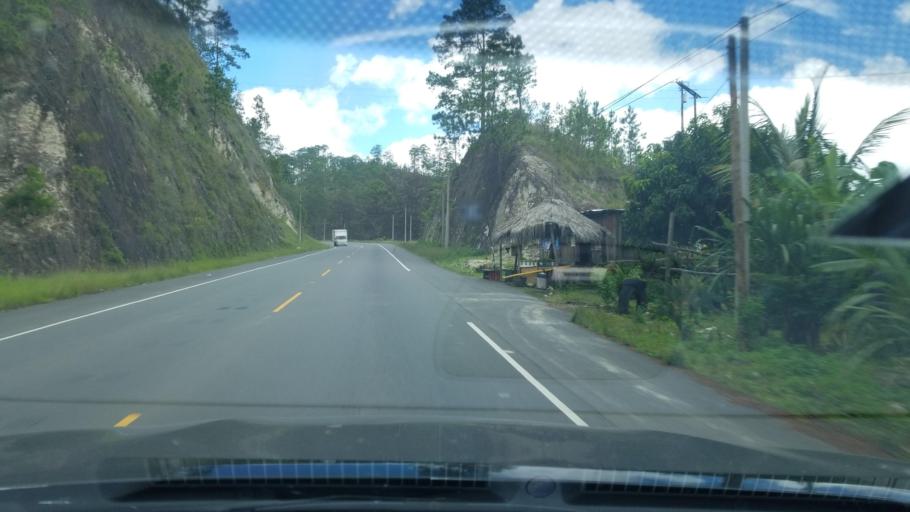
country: HN
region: Francisco Morazan
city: Talanga
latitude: 14.3598
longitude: -87.1465
